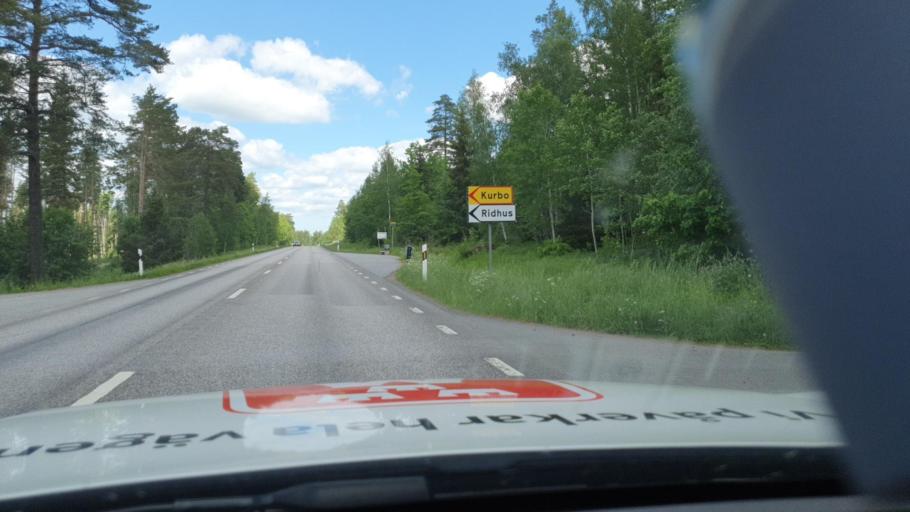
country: SE
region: Uppsala
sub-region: Uppsala Kommun
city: Vattholma
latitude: 60.0669
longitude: 17.7571
